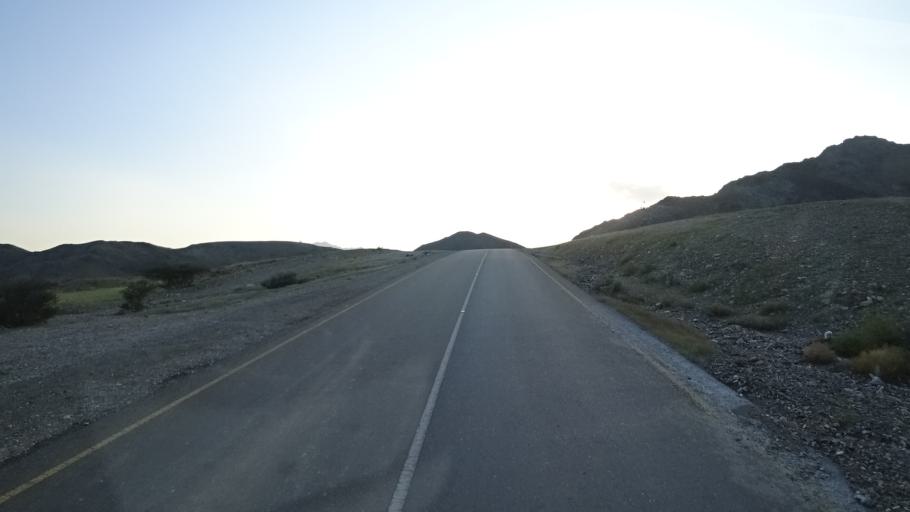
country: OM
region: Al Batinah
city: Al Khaburah
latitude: 23.7973
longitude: 56.9863
